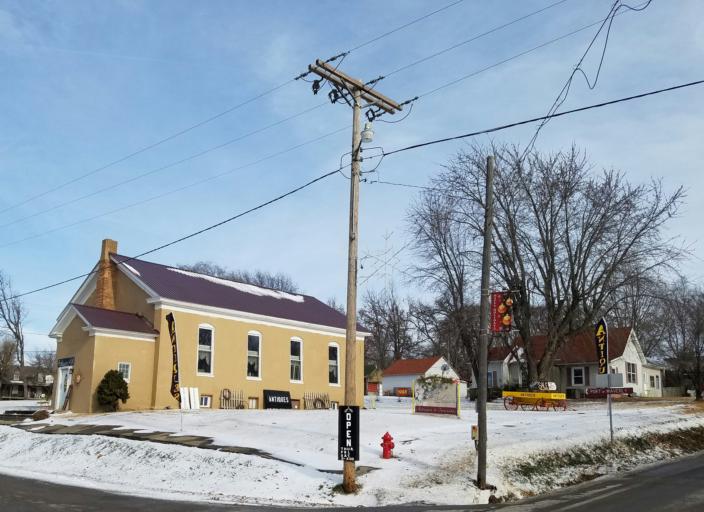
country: US
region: Missouri
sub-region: Carroll County
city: Carrollton
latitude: 39.2074
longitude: -93.5173
